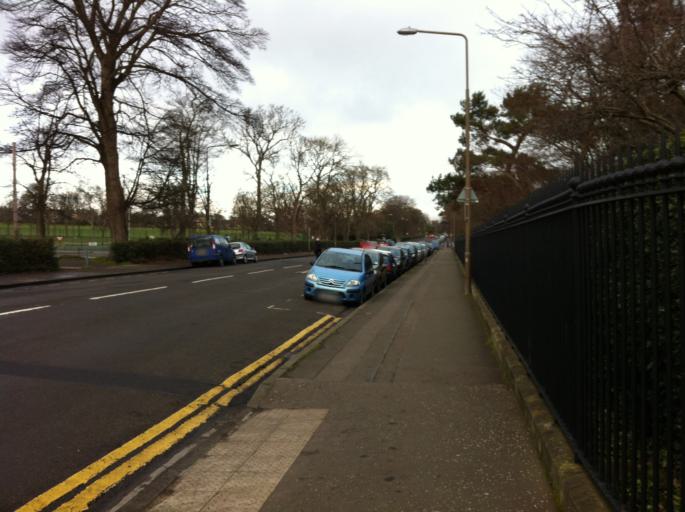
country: GB
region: Scotland
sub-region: Edinburgh
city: Edinburgh
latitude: 55.9628
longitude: -3.2116
